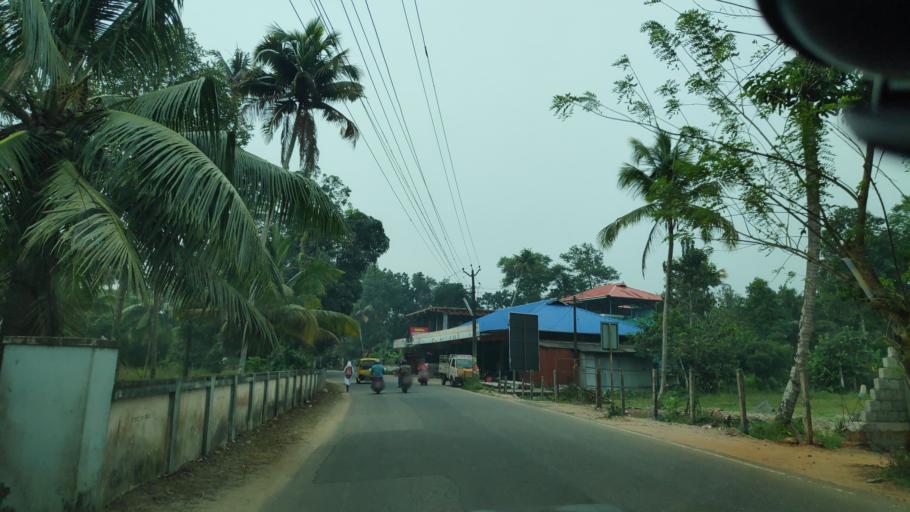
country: IN
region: Kerala
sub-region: Alappuzha
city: Alleppey
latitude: 9.5798
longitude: 76.3493
